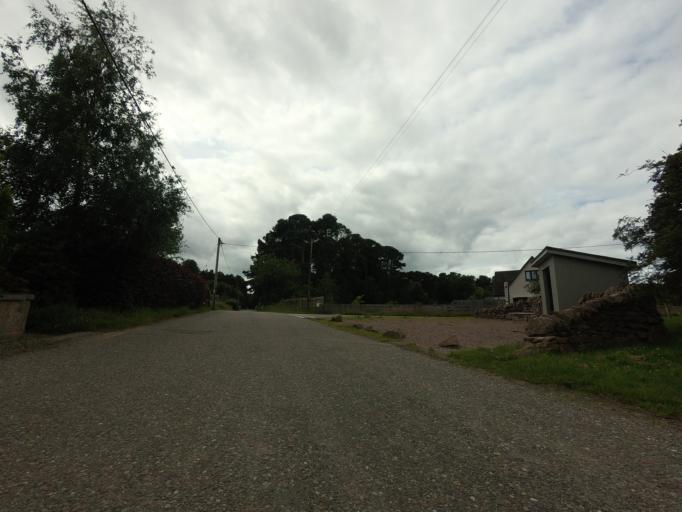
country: GB
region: Scotland
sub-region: Moray
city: Forres
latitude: 57.6214
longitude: -3.6734
